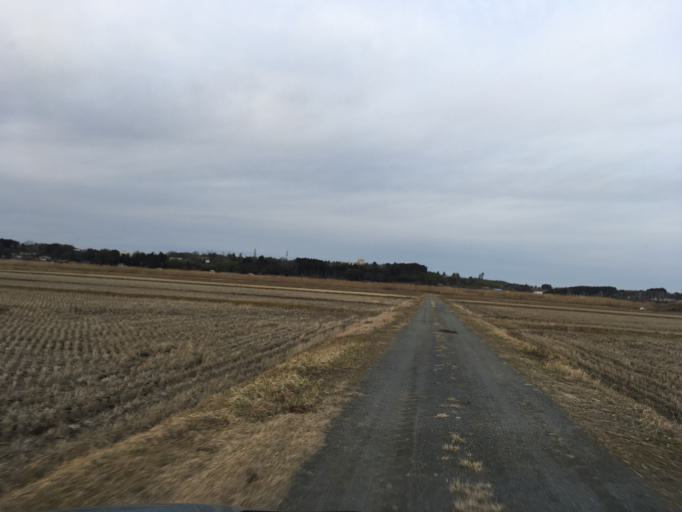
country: JP
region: Miyagi
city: Kogota
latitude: 38.6428
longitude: 141.0683
